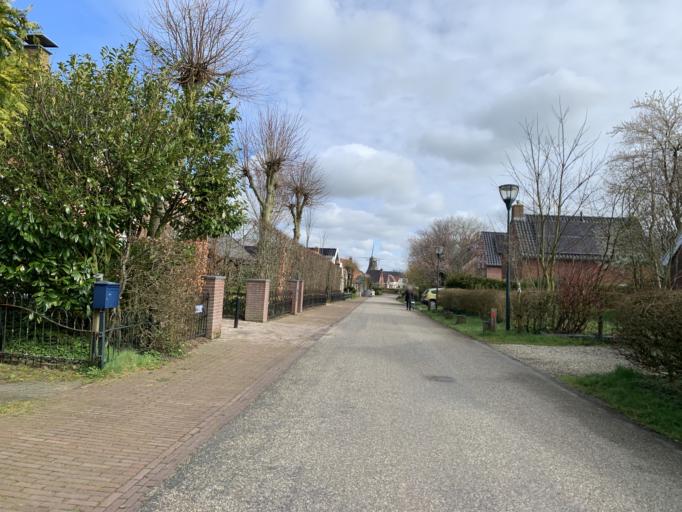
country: NL
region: Groningen
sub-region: Gemeente Groningen
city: Korrewegwijk
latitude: 53.2741
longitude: 6.5319
